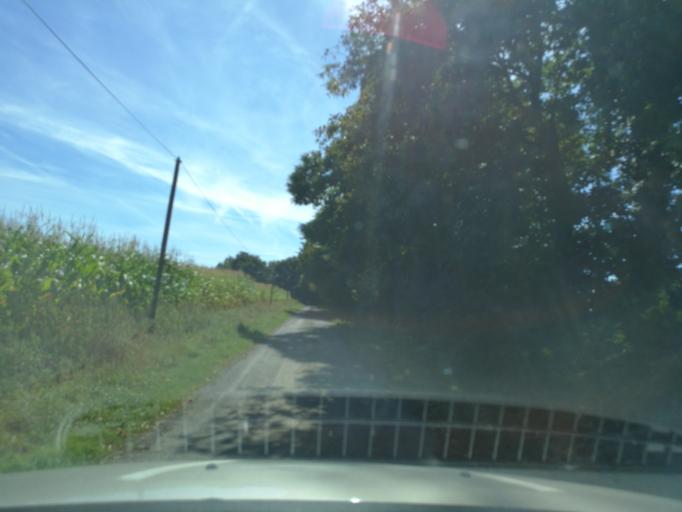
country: FR
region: Brittany
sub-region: Departement d'Ille-et-Vilaine
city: Bedee
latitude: 48.1595
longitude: -1.9551
